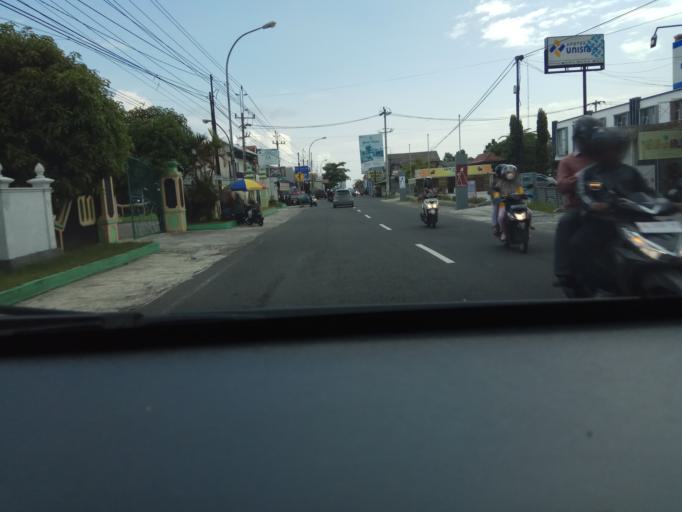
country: ID
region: Daerah Istimewa Yogyakarta
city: Melati
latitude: -7.7179
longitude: 110.4050
